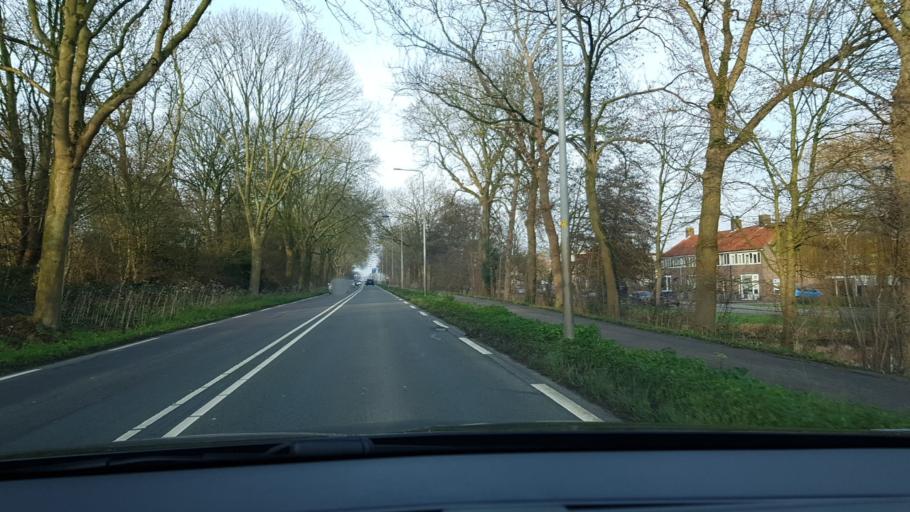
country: NL
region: North Holland
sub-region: Gemeente Uithoorn
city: Uithoorn
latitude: 52.2380
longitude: 4.8217
